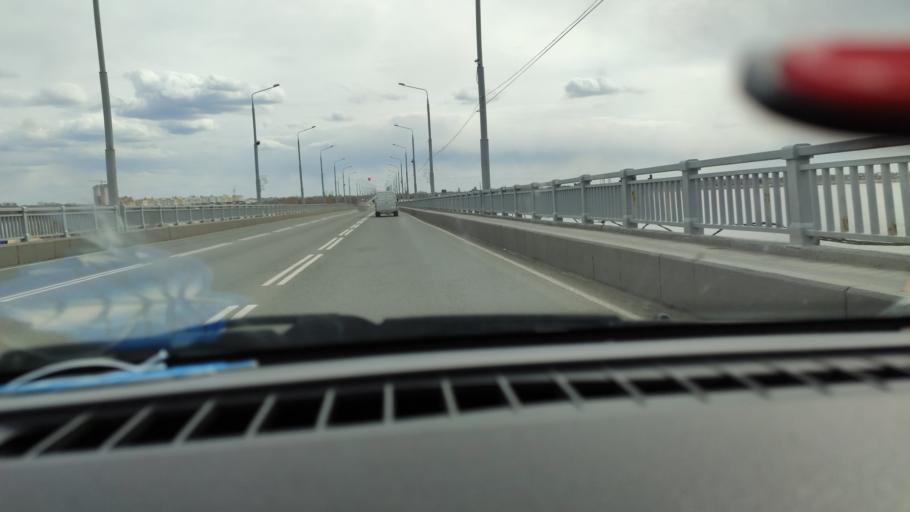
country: RU
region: Saratov
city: Engel's
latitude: 51.5138
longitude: 46.0724
